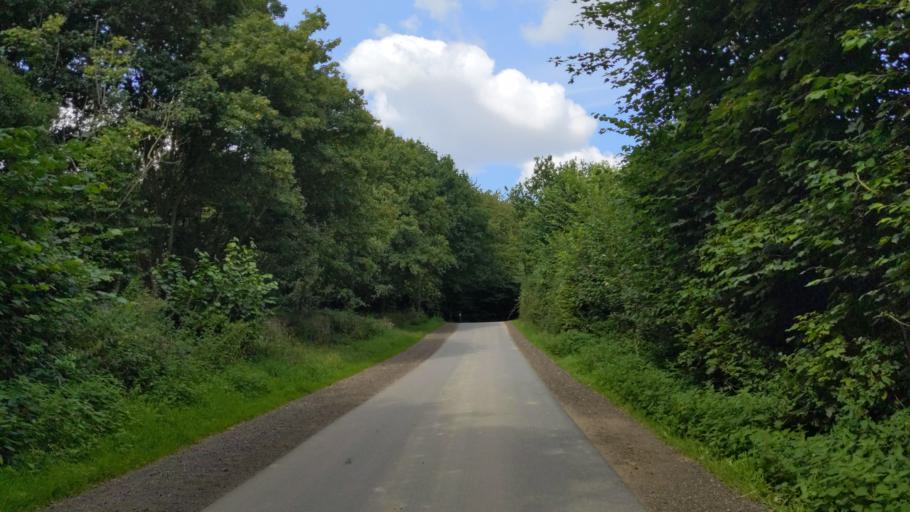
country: DE
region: Schleswig-Holstein
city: Neustadt in Holstein
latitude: 54.1412
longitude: 10.7929
